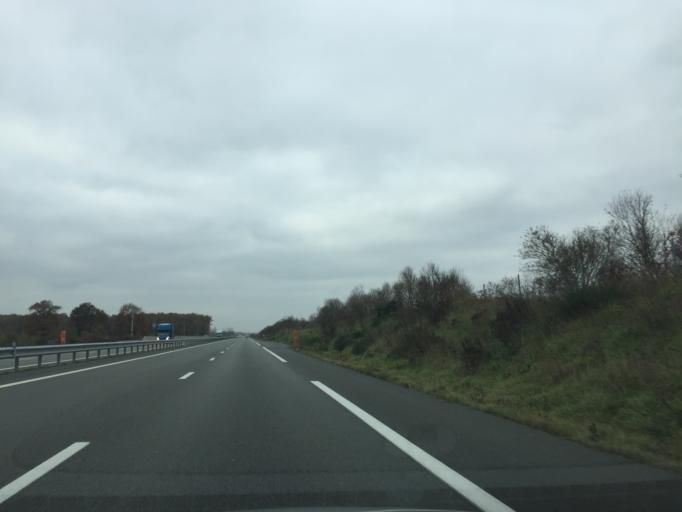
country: FR
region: Limousin
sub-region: Departement de la Creuse
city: Gouzon
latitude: 46.2147
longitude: 2.2828
